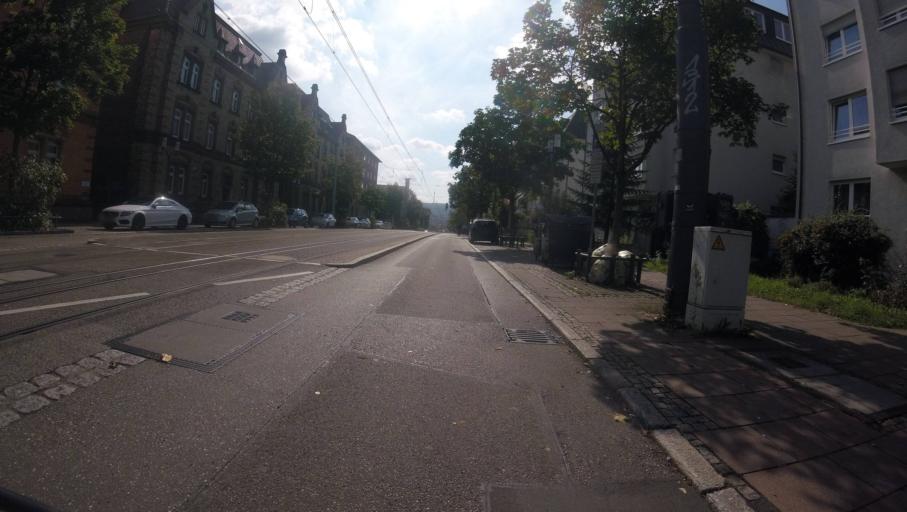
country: DE
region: Baden-Wuerttemberg
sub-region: Regierungsbezirk Stuttgart
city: Stuttgart
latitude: 48.7963
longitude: 9.1900
